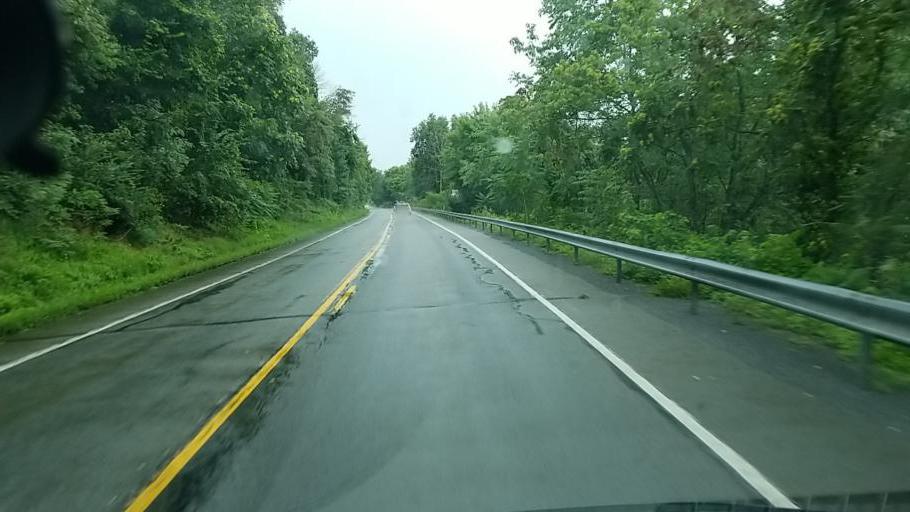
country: US
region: Pennsylvania
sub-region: Dauphin County
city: Millersburg
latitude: 40.5175
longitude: -76.9711
